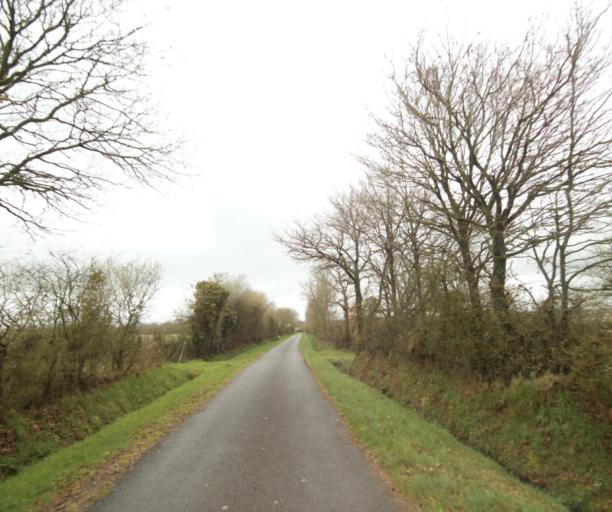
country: FR
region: Pays de la Loire
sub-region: Departement de la Loire-Atlantique
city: Quilly
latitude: 47.4575
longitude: -1.9007
